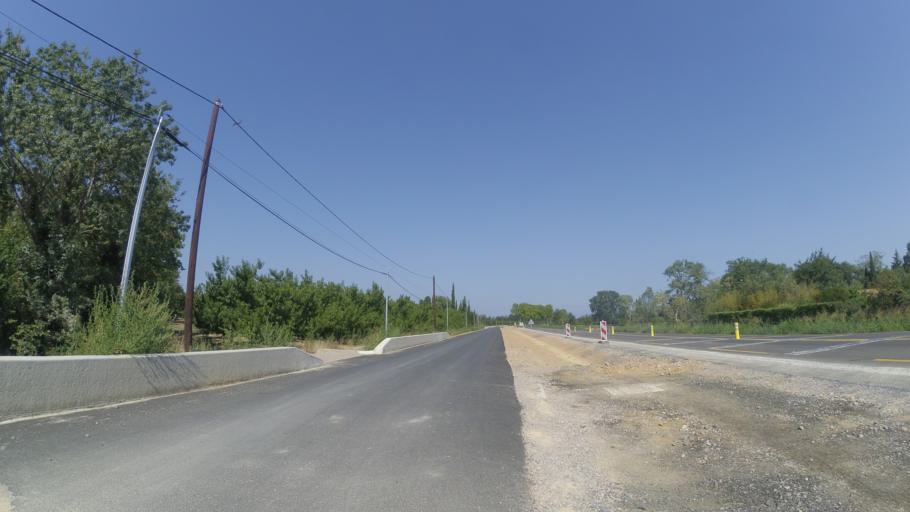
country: FR
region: Languedoc-Roussillon
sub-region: Departement des Pyrenees-Orientales
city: Thuir
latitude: 42.6438
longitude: 2.7406
